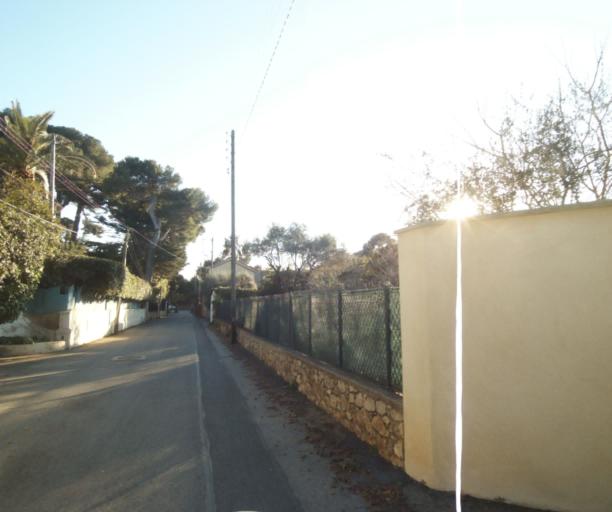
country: FR
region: Provence-Alpes-Cote d'Azur
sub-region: Departement des Alpes-Maritimes
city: Antibes
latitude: 43.5500
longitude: 7.1268
